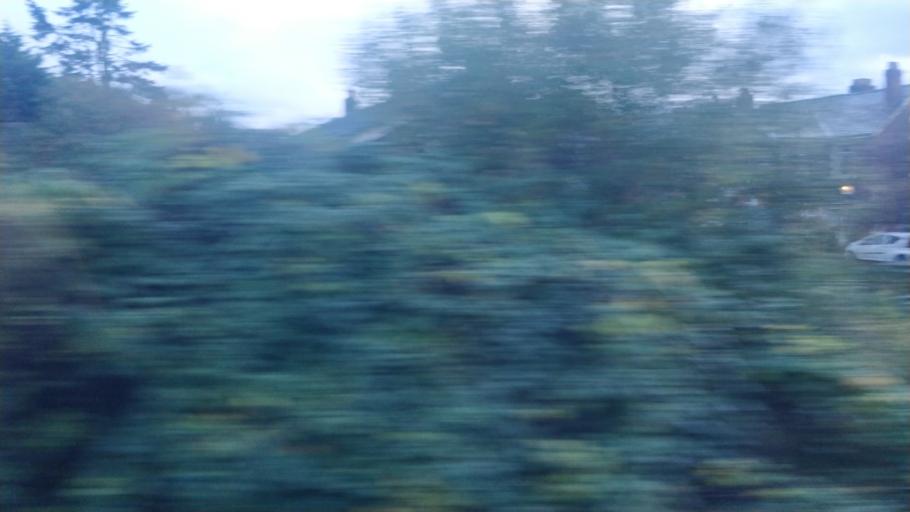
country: GB
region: England
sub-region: Lancashire
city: Parbold
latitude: 53.5904
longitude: -2.7699
